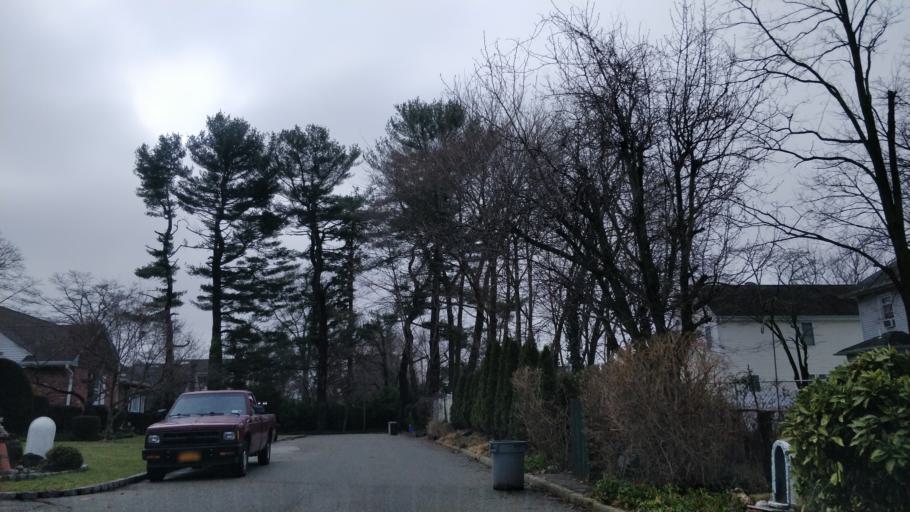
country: US
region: New York
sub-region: Nassau County
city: Glen Cove
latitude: 40.8589
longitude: -73.6133
